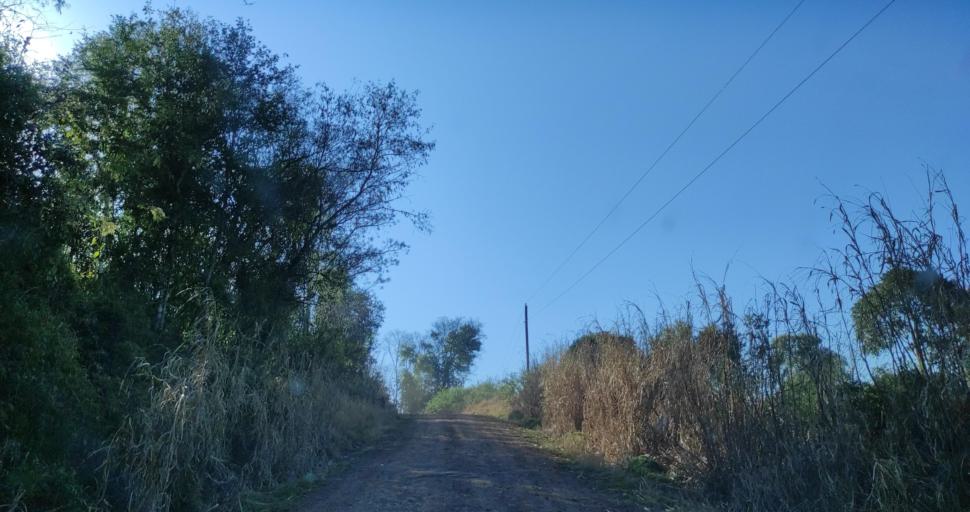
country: AR
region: Misiones
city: Capiovi
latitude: -26.8962
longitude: -55.0931
